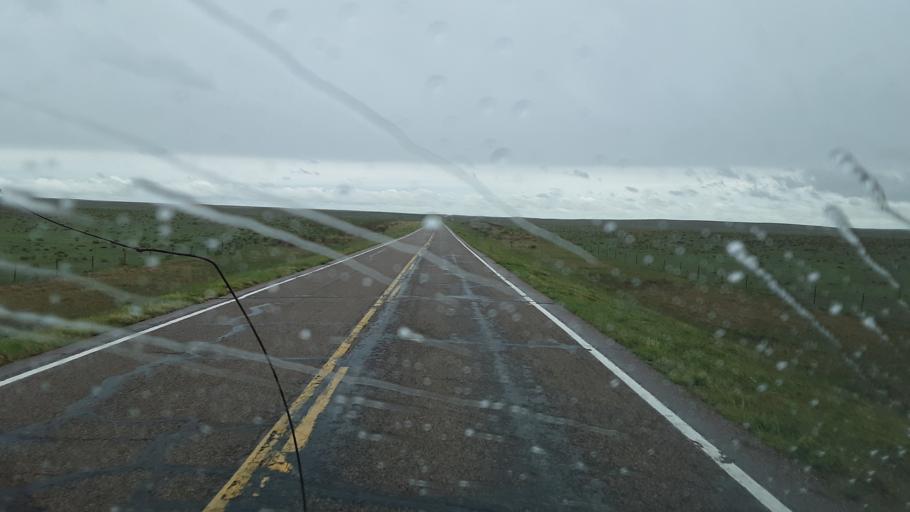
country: US
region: Colorado
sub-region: Lincoln County
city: Hugo
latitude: 38.8497
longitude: -103.2059
